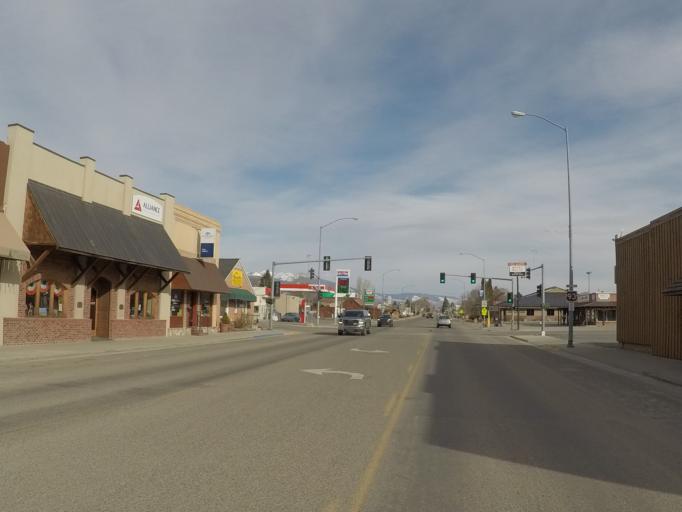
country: US
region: Idaho
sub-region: Lemhi County
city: Salmon
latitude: 45.1752
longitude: -113.8928
